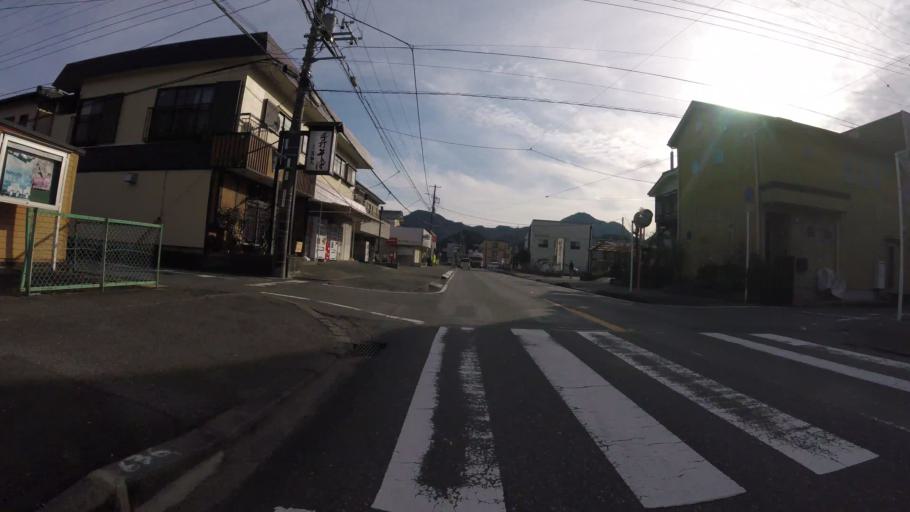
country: JP
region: Shizuoka
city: Mishima
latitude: 35.0846
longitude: 138.8996
